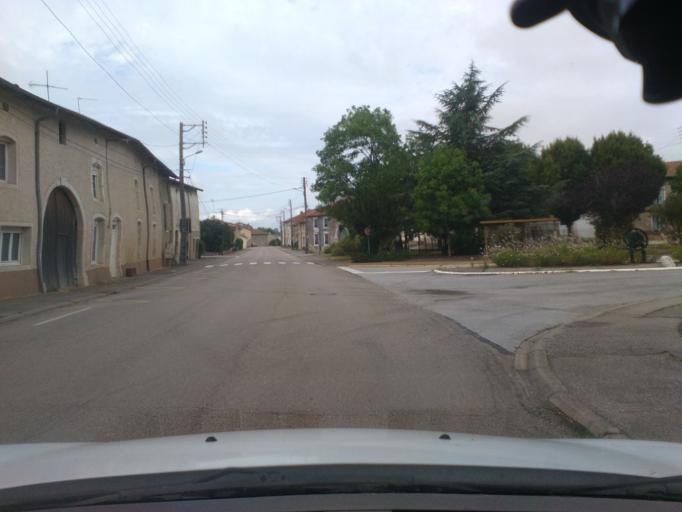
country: FR
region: Lorraine
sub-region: Departement de Meurthe-et-Moselle
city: Vezelise
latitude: 48.4192
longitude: 6.1319
